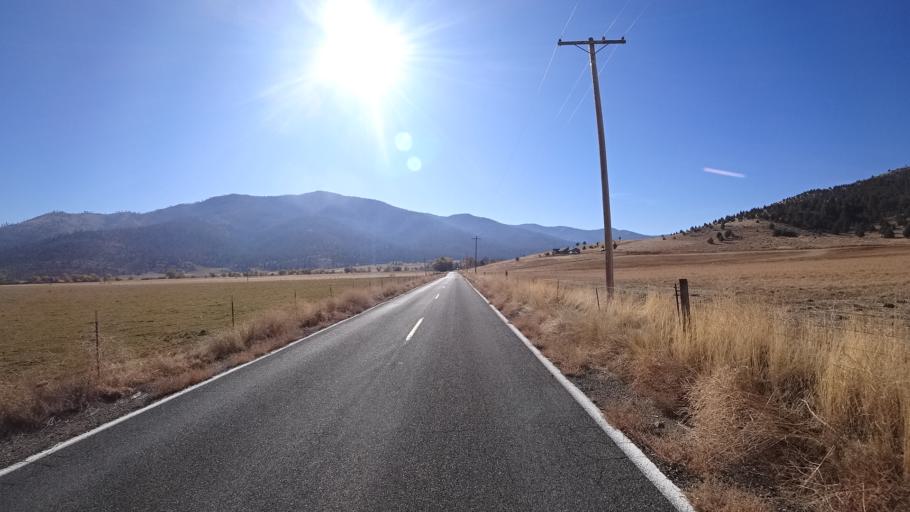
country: US
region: California
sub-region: Siskiyou County
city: Weed
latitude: 41.4993
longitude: -122.5505
